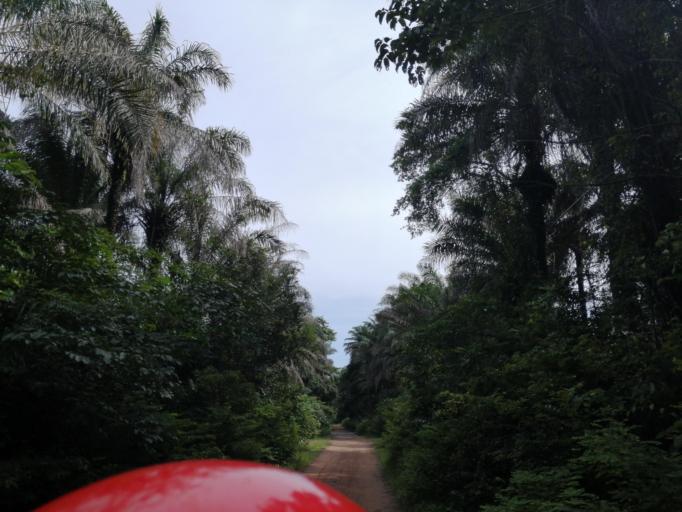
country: SL
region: Northern Province
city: Mange
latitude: 8.8060
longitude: -12.9267
